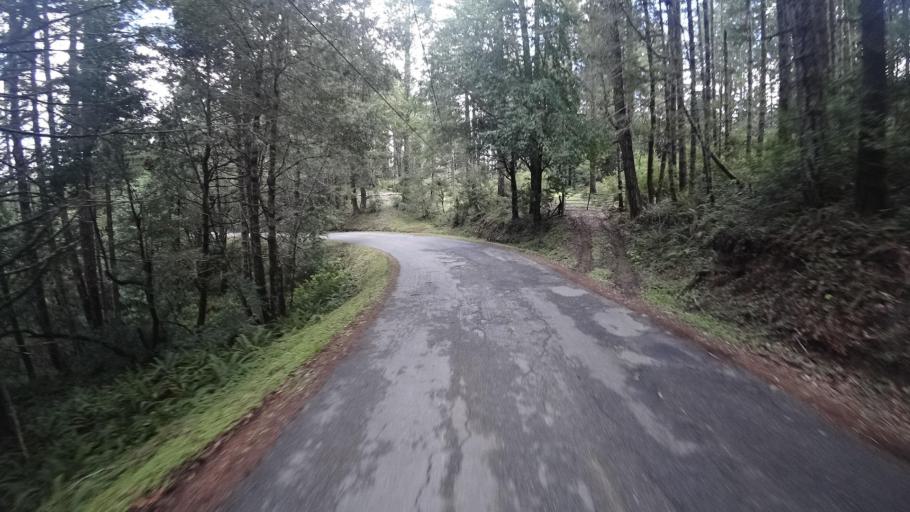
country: US
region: California
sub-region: Humboldt County
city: Bayside
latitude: 40.7559
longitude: -123.9703
